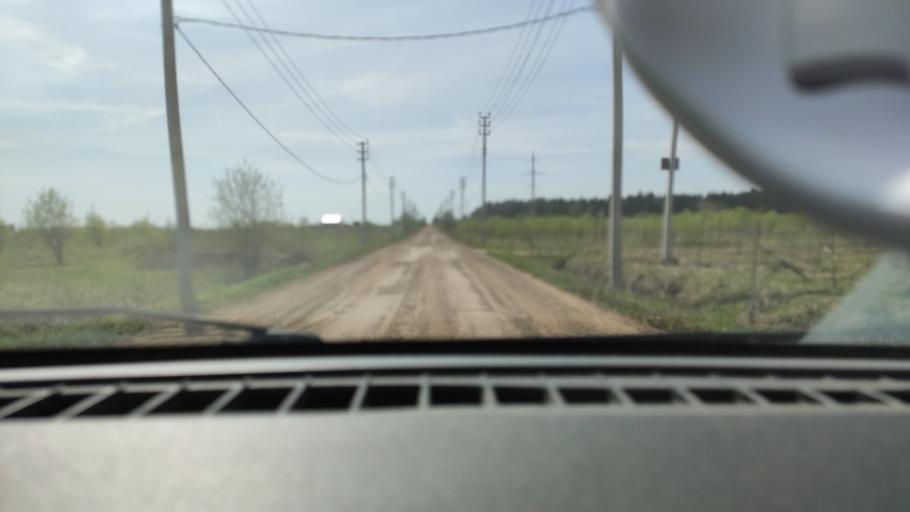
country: RU
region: Perm
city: Kultayevo
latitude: 57.8894
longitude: 55.8621
